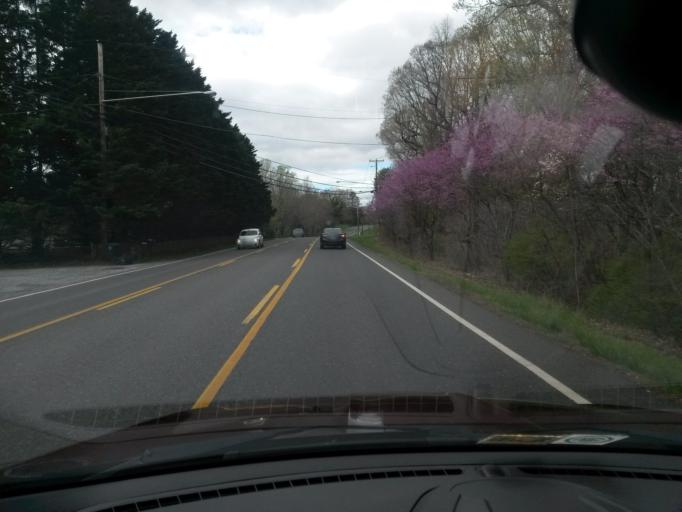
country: US
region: Virginia
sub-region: City of Lynchburg
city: West Lynchburg
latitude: 37.4465
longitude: -79.2514
